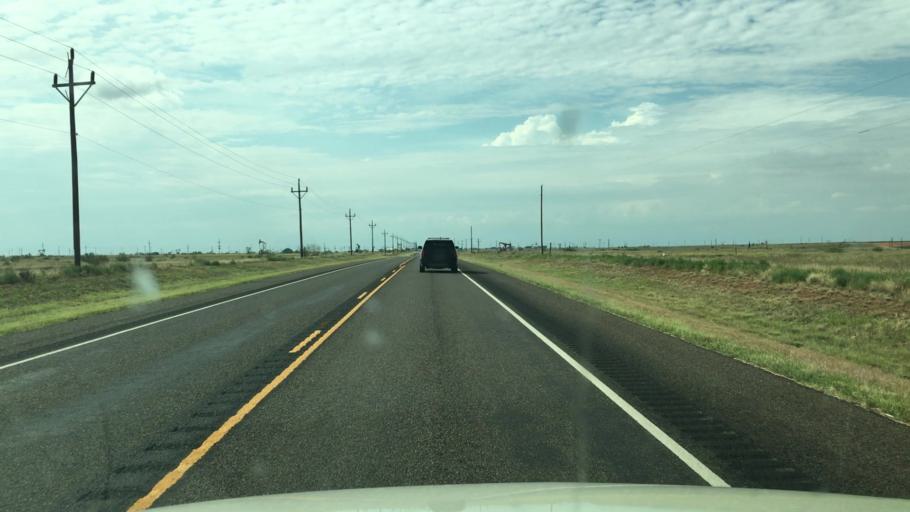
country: US
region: Texas
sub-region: Dawson County
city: Lamesa
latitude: 32.8914
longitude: -102.0908
